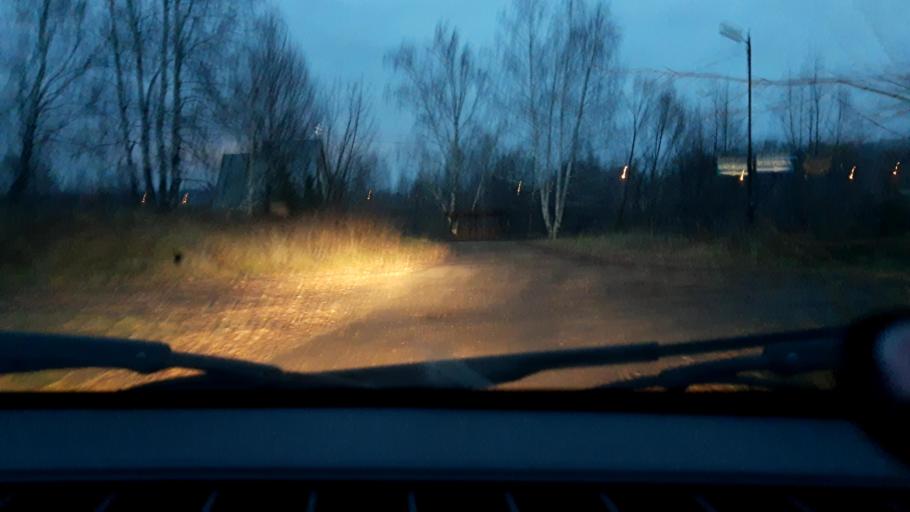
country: RU
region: Bashkortostan
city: Mikhaylovka
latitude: 54.8338
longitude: 55.8566
